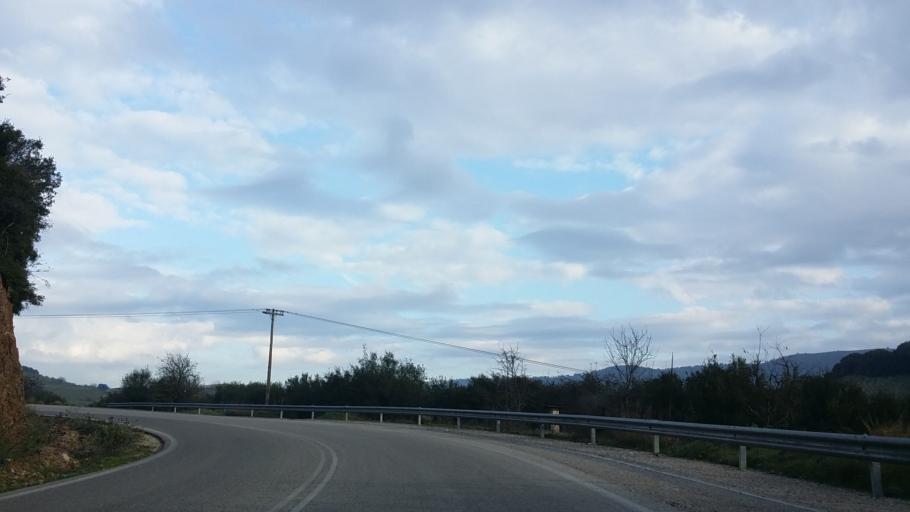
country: GR
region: West Greece
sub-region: Nomos Aitolias kai Akarnanias
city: Katouna
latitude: 38.7792
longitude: 21.1246
